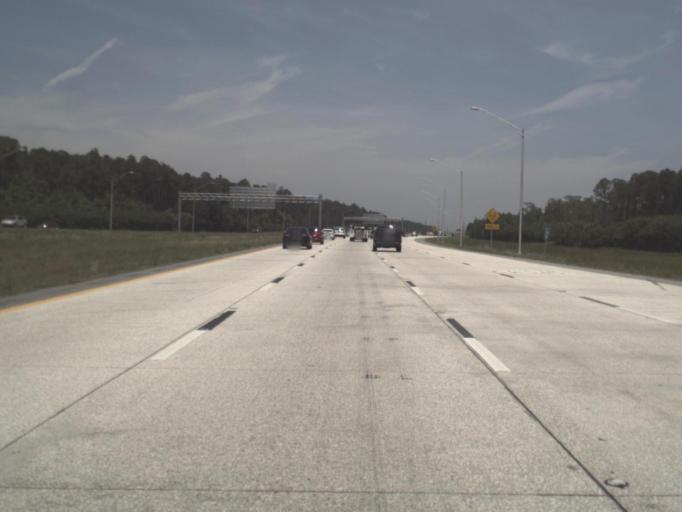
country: US
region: Florida
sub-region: Saint Johns County
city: Palm Valley
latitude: 30.1834
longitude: -81.5132
